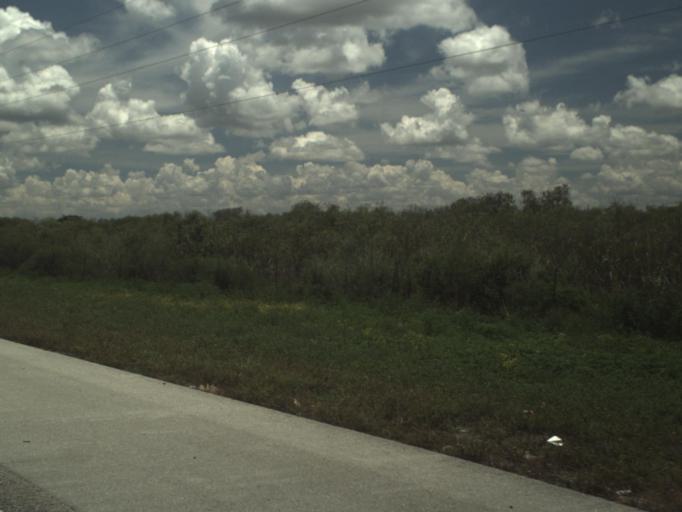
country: US
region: Florida
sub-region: Broward County
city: Weston
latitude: 26.1515
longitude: -80.7331
